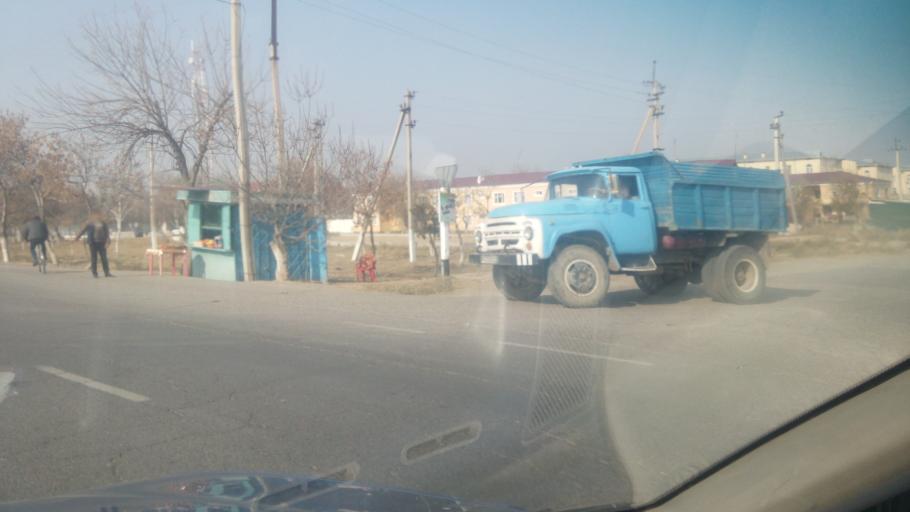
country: UZ
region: Sirdaryo
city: Guliston
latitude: 40.4886
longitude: 68.7501
